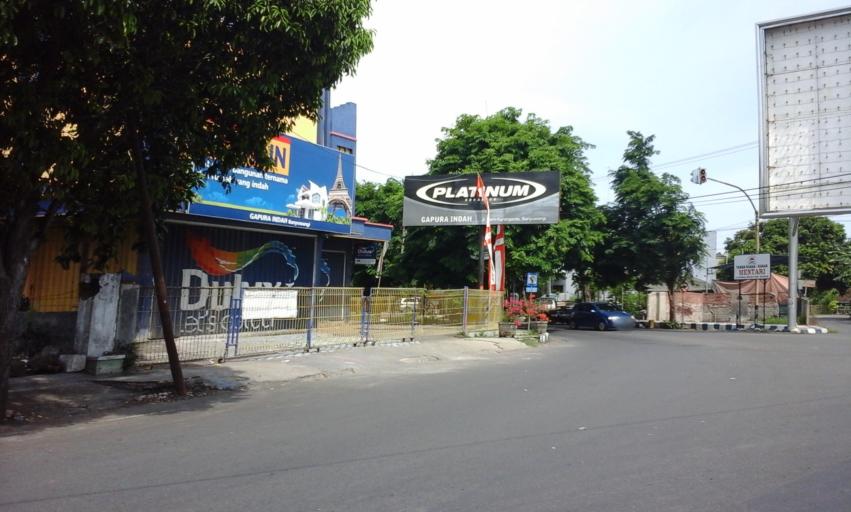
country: ID
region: East Java
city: Banyuwangi
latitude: -8.2366
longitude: 114.3586
